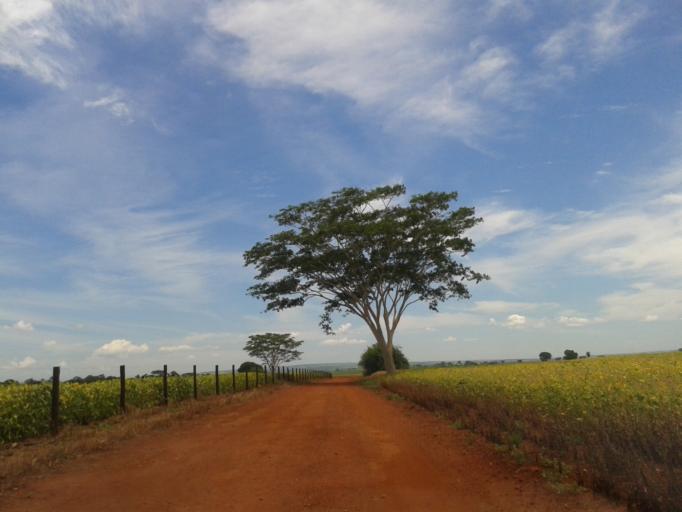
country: BR
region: Minas Gerais
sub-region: Capinopolis
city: Capinopolis
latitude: -18.6671
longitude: -49.7270
